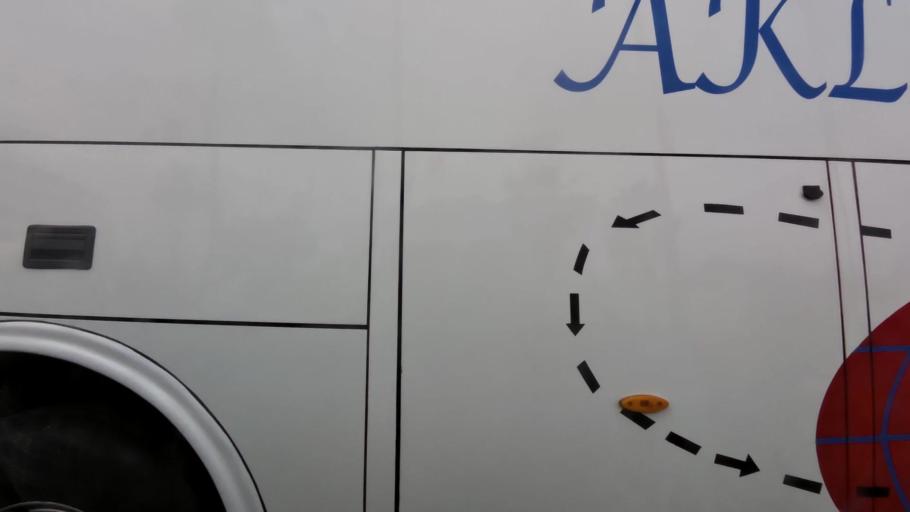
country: MA
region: Grand Casablanca
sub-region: Casablanca
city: Casablanca
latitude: 33.5919
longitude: -7.6776
